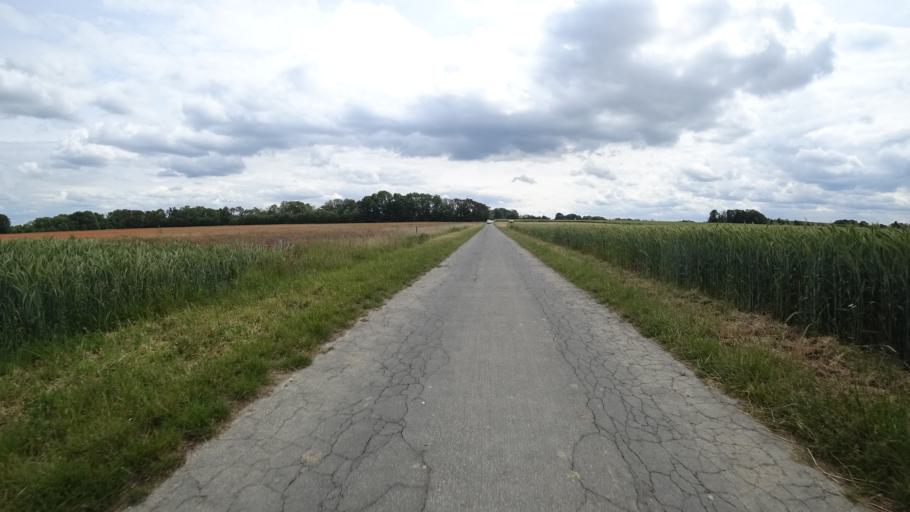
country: DE
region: North Rhine-Westphalia
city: Erwitte
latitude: 51.6085
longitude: 8.3959
